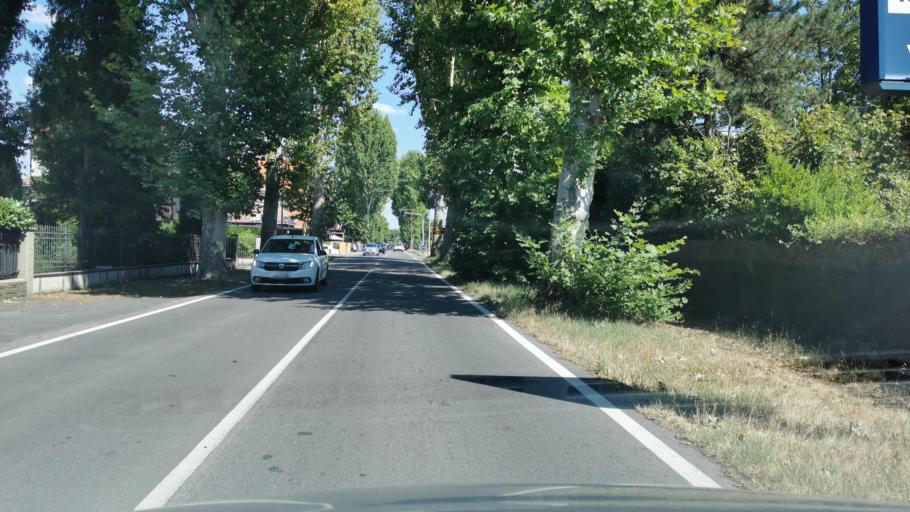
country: IT
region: Emilia-Romagna
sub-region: Provincia di Modena
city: Limidi
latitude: 44.7648
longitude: 10.9201
